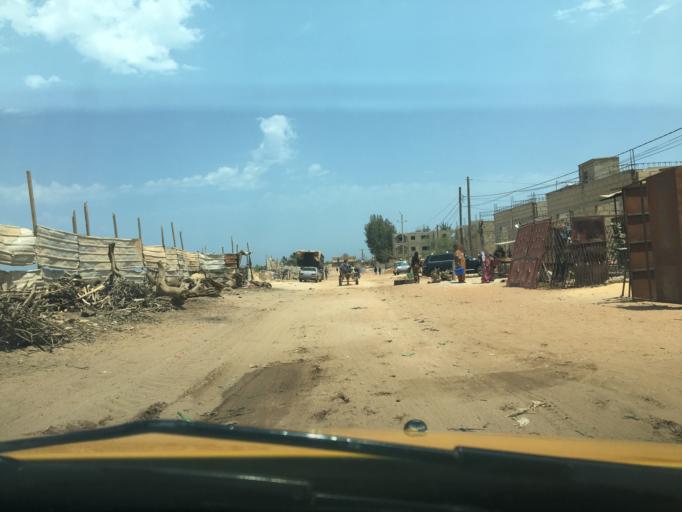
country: SN
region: Thies
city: Thies
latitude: 14.8043
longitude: -17.1860
